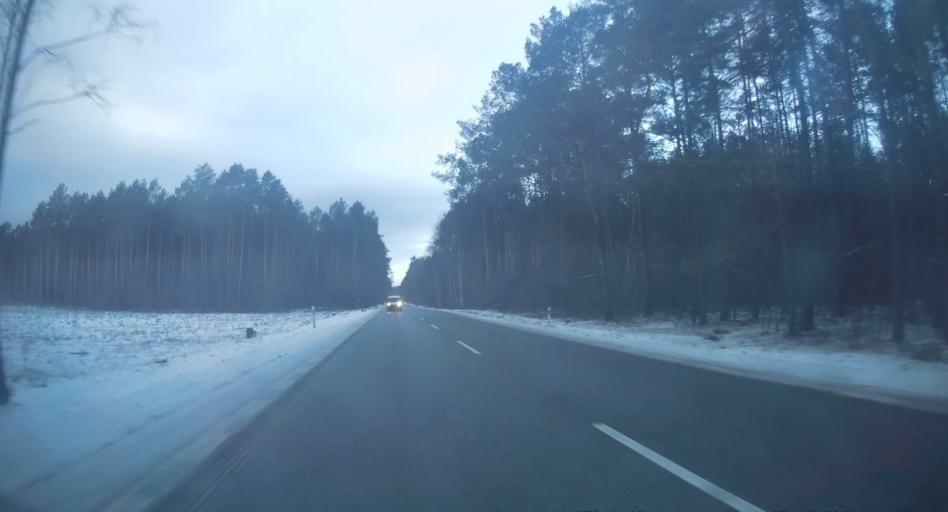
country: PL
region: Swietokrzyskie
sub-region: Powiat konecki
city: Smykow
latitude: 51.0916
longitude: 20.3541
